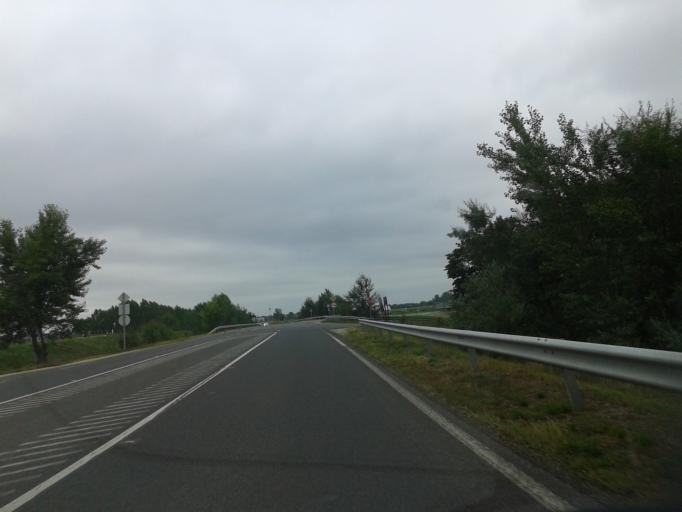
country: HU
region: Bacs-Kiskun
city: Solt
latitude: 46.7797
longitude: 19.0057
